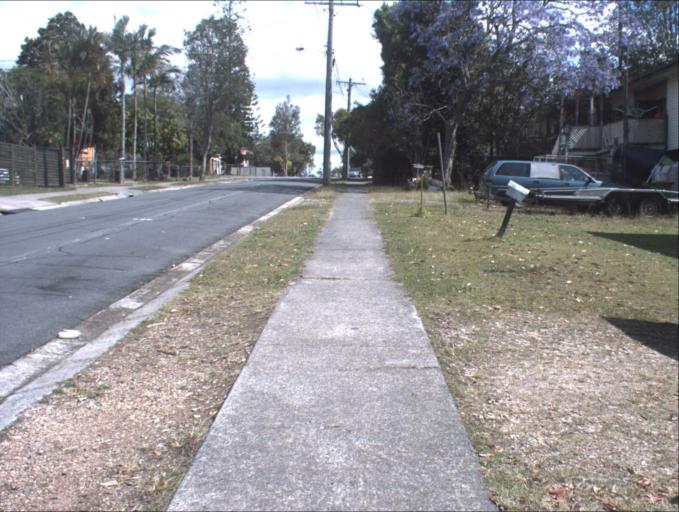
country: AU
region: Queensland
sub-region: Logan
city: Logan City
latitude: -27.6471
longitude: 153.1139
